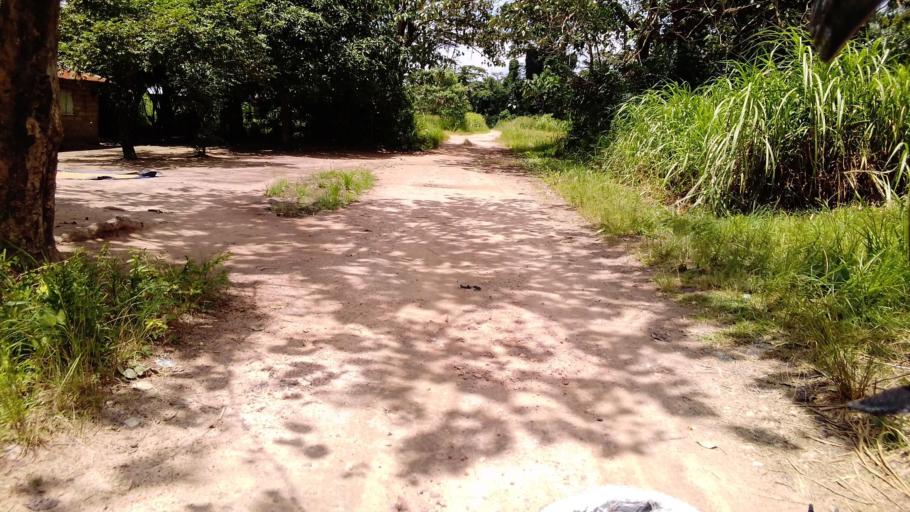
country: SL
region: Eastern Province
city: Koidu
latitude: 8.6947
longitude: -10.9539
